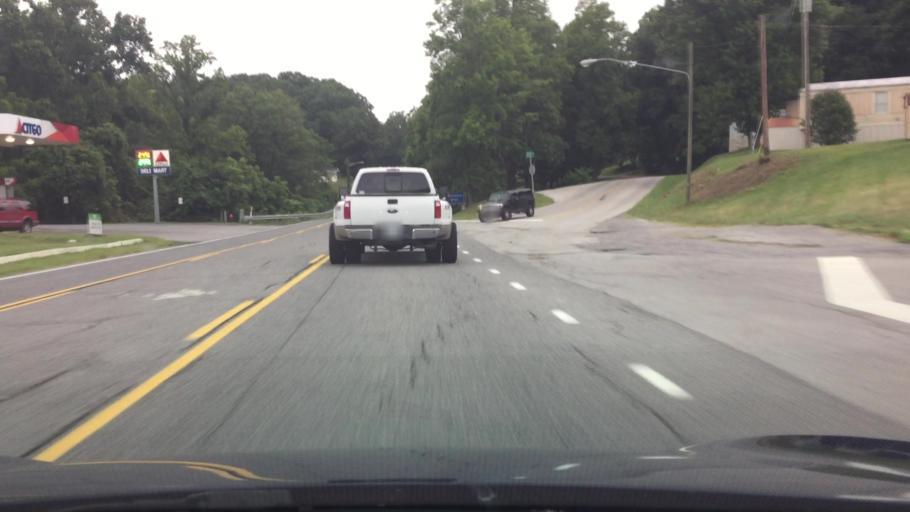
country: US
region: Virginia
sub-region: Montgomery County
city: Shawsville
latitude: 37.1405
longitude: -80.3255
